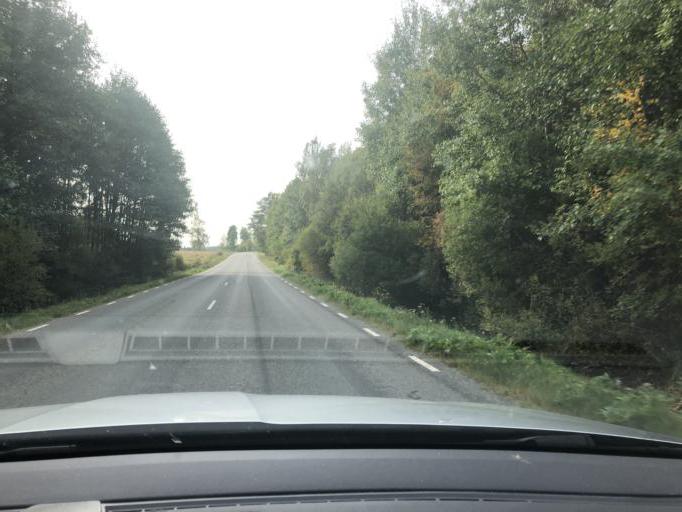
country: SE
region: Joenkoeping
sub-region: Vetlanda Kommun
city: Ekenassjon
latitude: 57.5285
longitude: 14.9412
